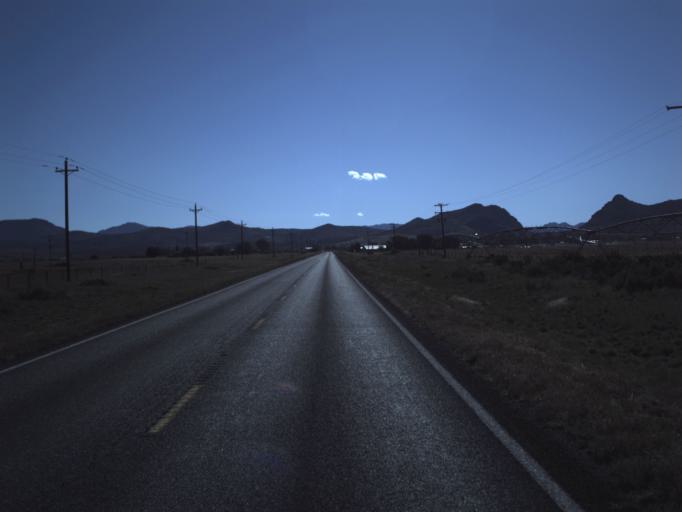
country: US
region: Utah
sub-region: Washington County
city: Enterprise
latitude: 37.6782
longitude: -113.5694
